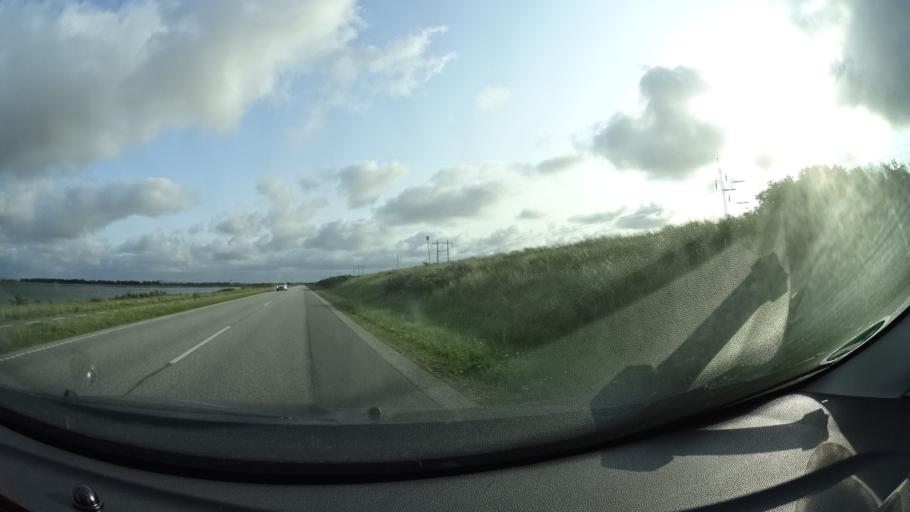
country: DK
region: Central Jutland
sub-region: Lemvig Kommune
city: Harboore
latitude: 56.6384
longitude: 8.1872
